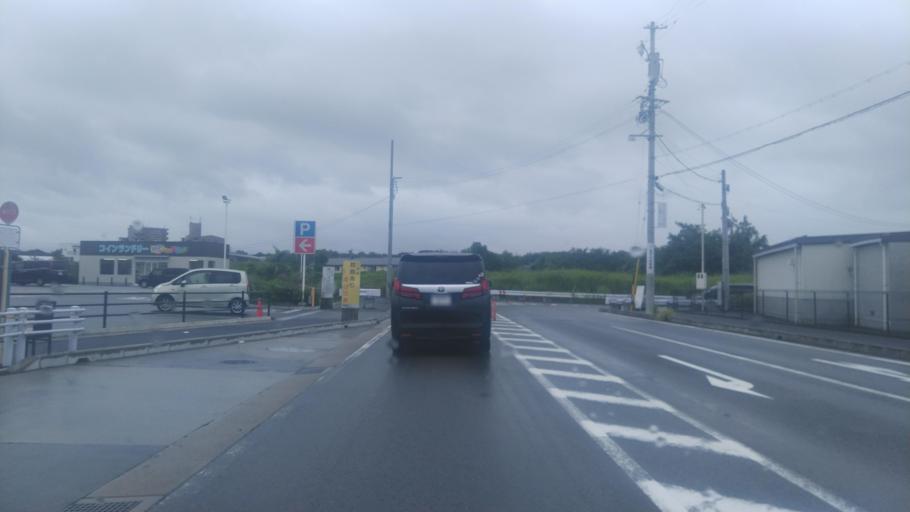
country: JP
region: Aichi
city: Kasugai
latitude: 35.2474
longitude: 137.0248
